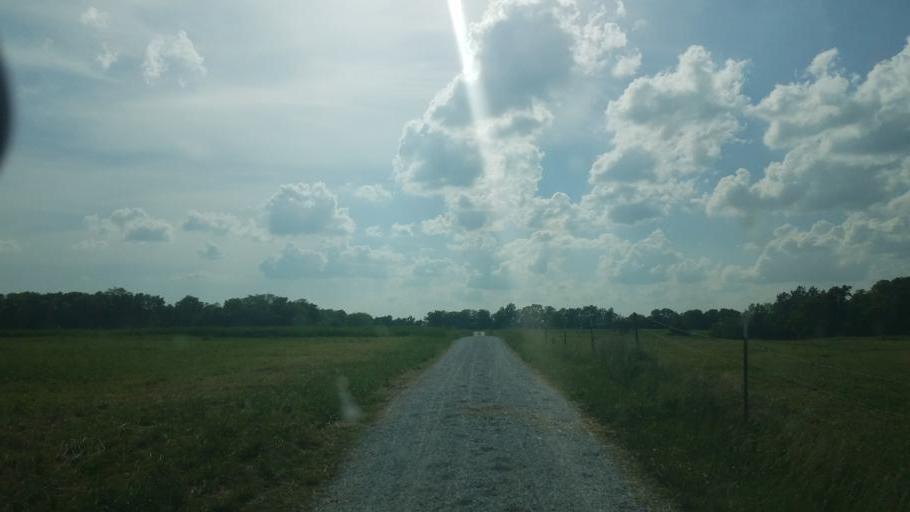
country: US
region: Missouri
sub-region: Cooper County
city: Boonville
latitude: 38.8558
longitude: -92.6477
